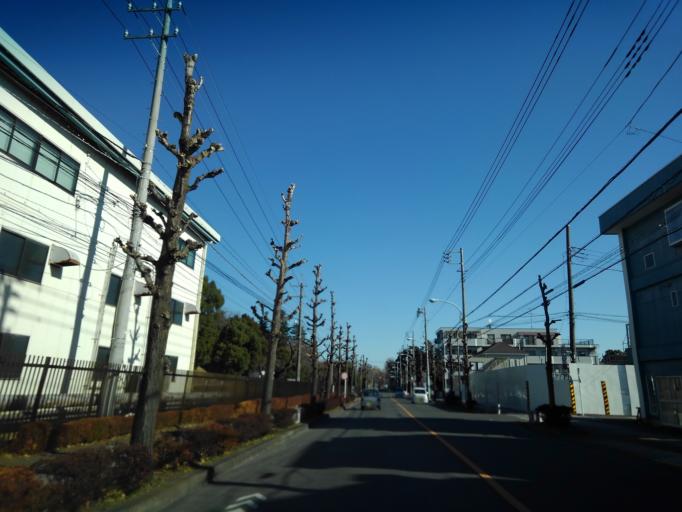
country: JP
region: Tokyo
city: Fussa
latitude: 35.7672
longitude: 139.3254
